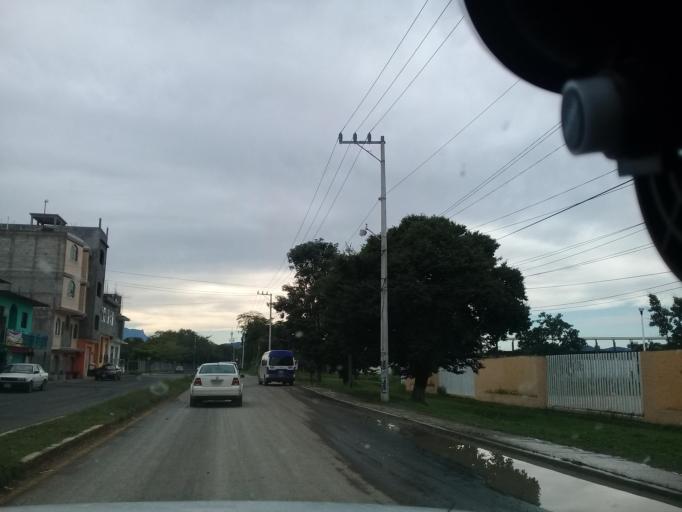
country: MX
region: Hidalgo
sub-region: Huejutla de Reyes
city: Parque de Poblamiento Solidaridad
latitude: 21.1549
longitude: -98.3814
